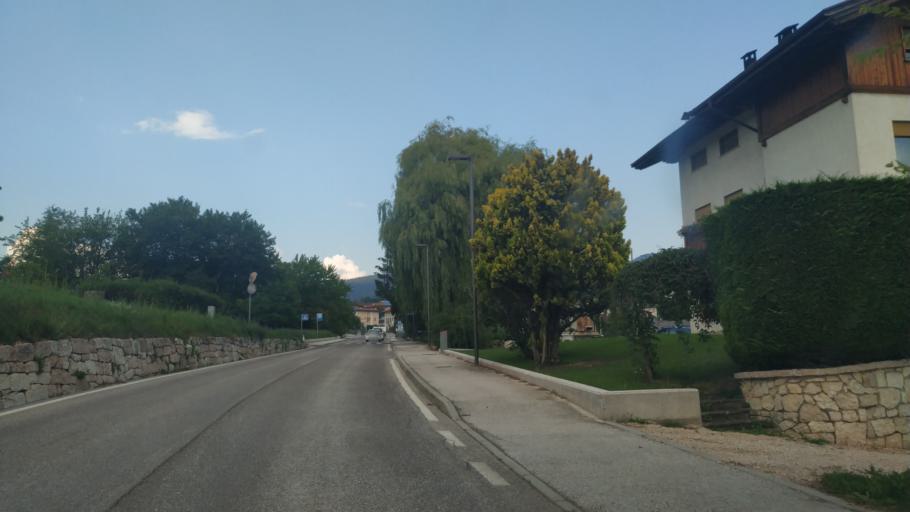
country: IT
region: Trentino-Alto Adige
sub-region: Provincia di Trento
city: Cavareno
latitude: 46.4047
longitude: 11.1339
